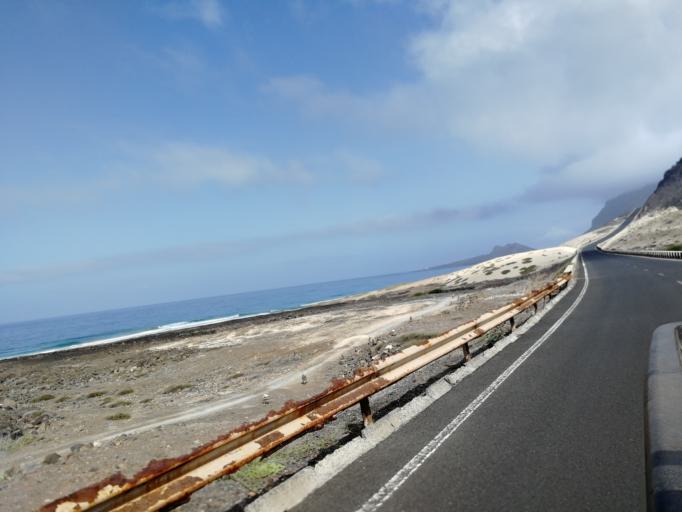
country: CV
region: Sao Vicente
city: Mindelo
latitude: 16.8733
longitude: -24.9083
